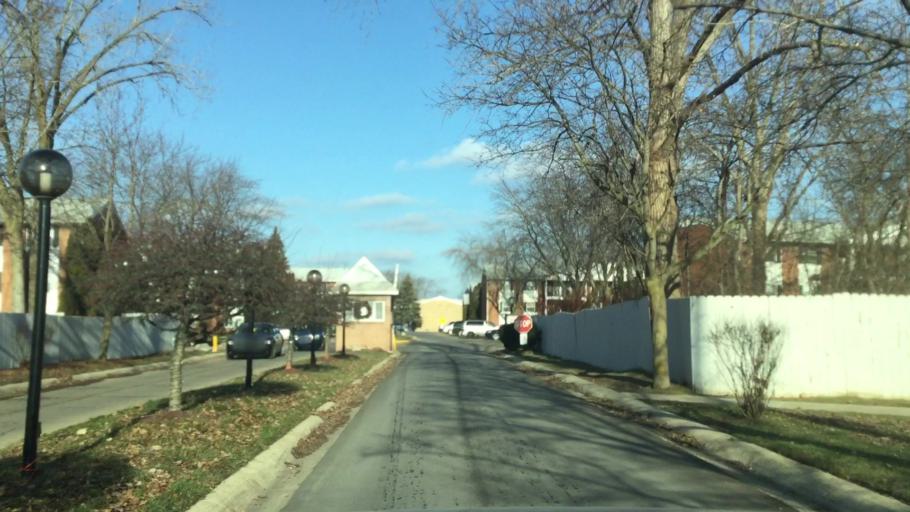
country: US
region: Michigan
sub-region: Genesee County
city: Flint
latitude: 43.0283
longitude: -83.7438
